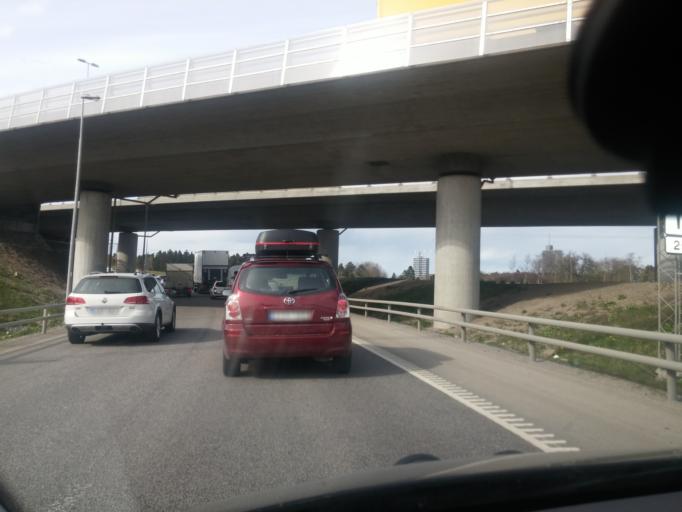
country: SE
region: Stockholm
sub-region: Stockholms Kommun
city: Kista
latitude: 59.3887
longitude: 17.9401
